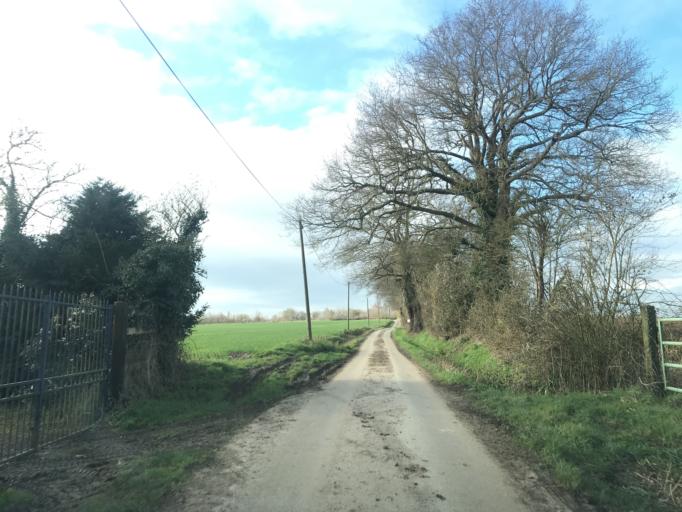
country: FR
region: Lower Normandy
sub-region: Departement du Calvados
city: Dives-sur-Mer
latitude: 49.2265
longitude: -0.1051
